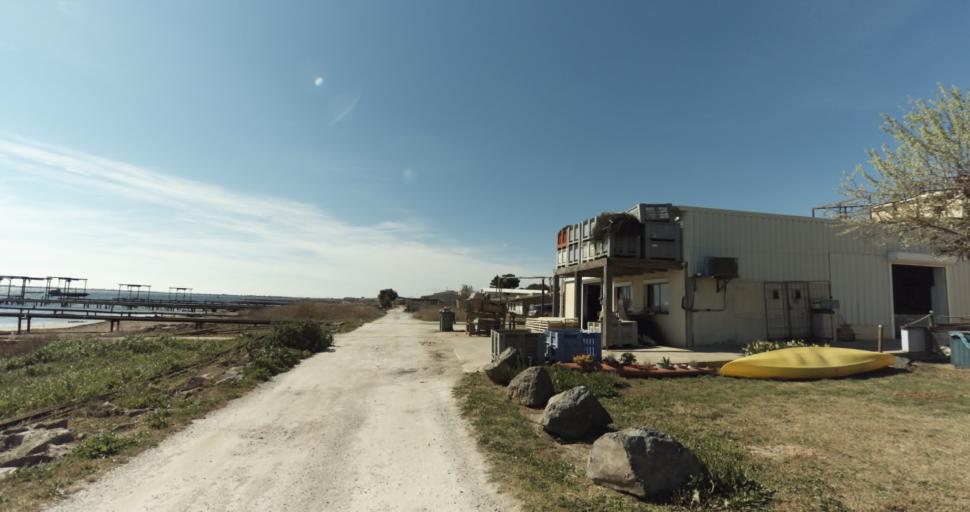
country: FR
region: Languedoc-Roussillon
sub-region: Departement de l'Herault
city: Marseillan
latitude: 43.3683
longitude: 3.5404
